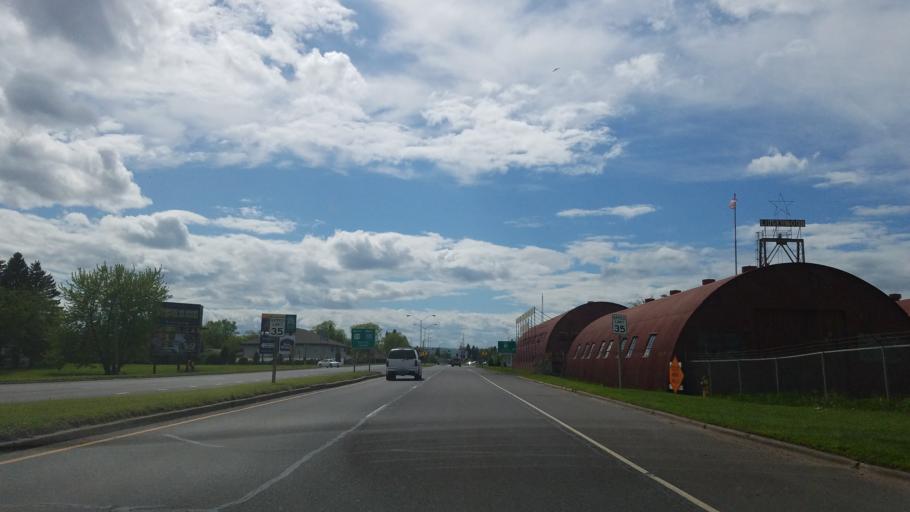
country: US
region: Wisconsin
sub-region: Douglas County
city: Superior
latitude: 46.7339
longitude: -92.0910
